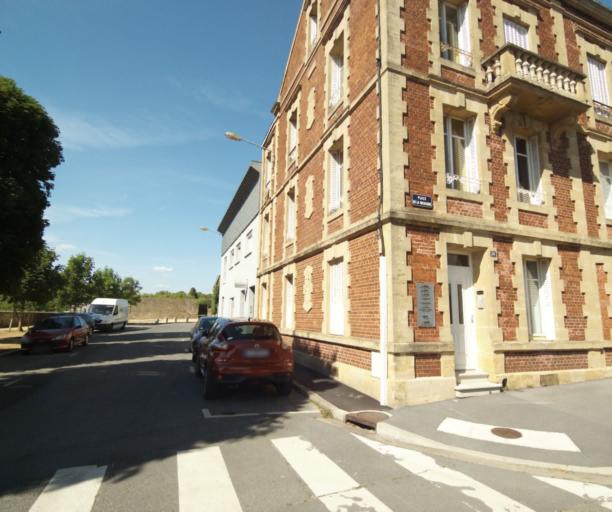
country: FR
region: Champagne-Ardenne
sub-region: Departement des Ardennes
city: Charleville-Mezieres
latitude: 49.7612
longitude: 4.7141
